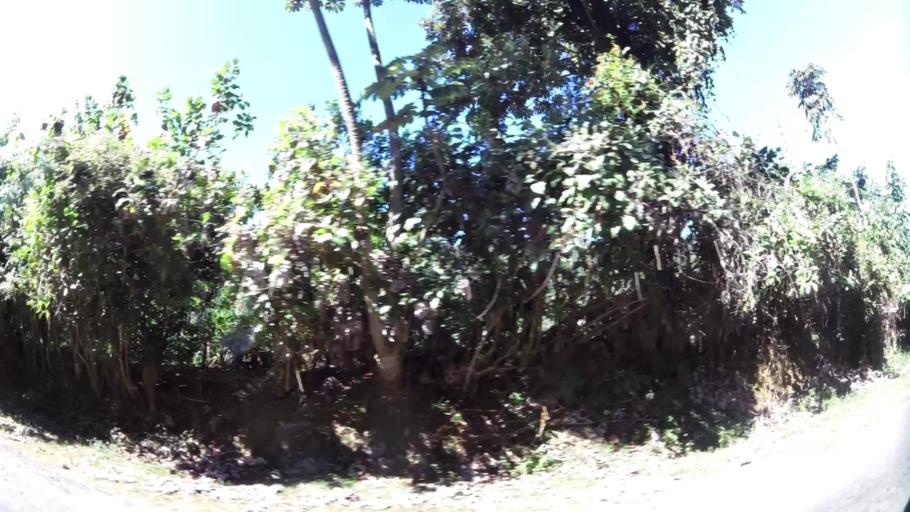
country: SV
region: Ahuachapan
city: Concepcion de Ataco
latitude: 13.8782
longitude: -89.8444
